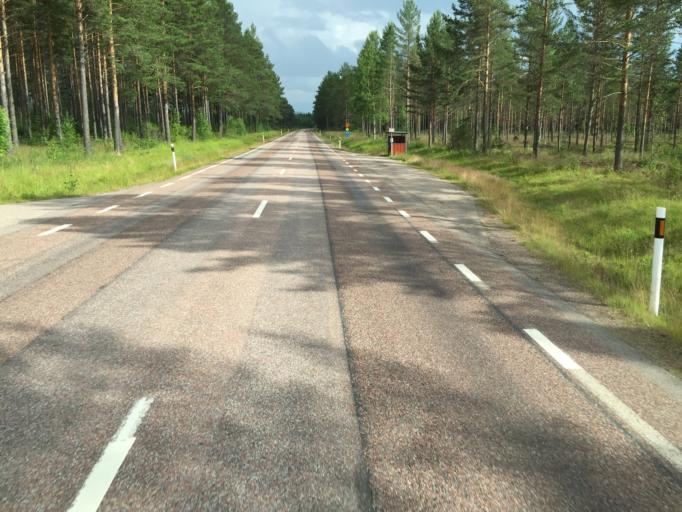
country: SE
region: Dalarna
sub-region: Vansbro Kommun
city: Jarna
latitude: 60.5355
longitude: 14.4278
